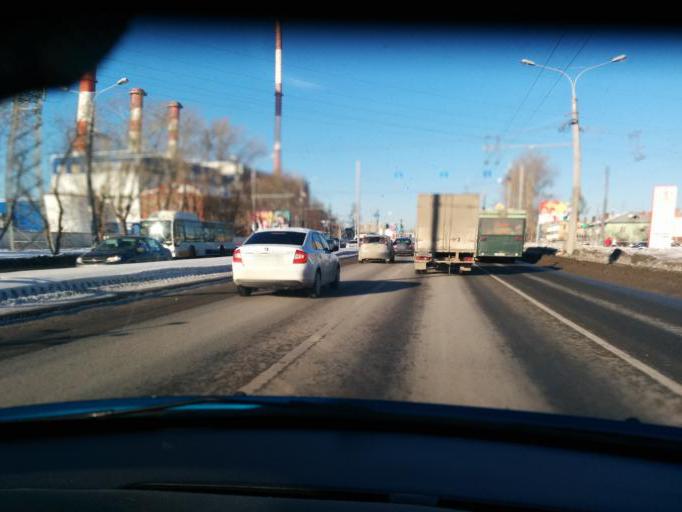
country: RU
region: Perm
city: Perm
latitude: 57.9758
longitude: 56.2597
